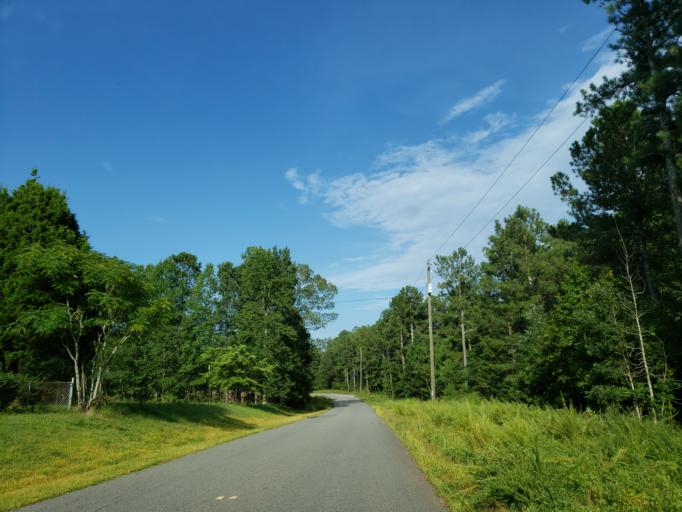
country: US
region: Georgia
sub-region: Bartow County
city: Emerson
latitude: 34.1909
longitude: -84.6507
